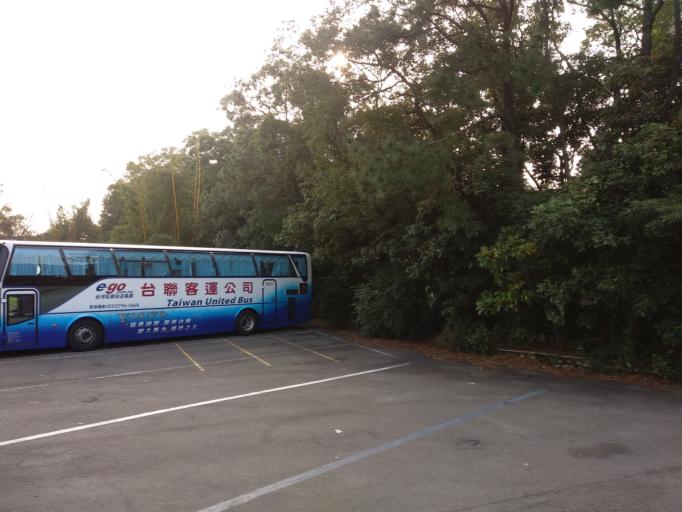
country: TW
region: Taiwan
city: Daxi
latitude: 24.8236
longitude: 121.1833
